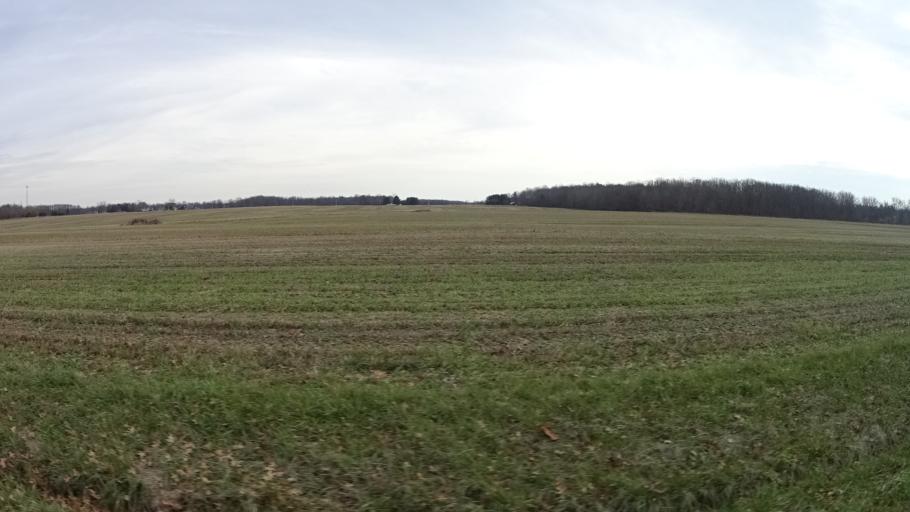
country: US
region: Ohio
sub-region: Lorain County
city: Wellington
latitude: 41.1944
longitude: -82.1687
